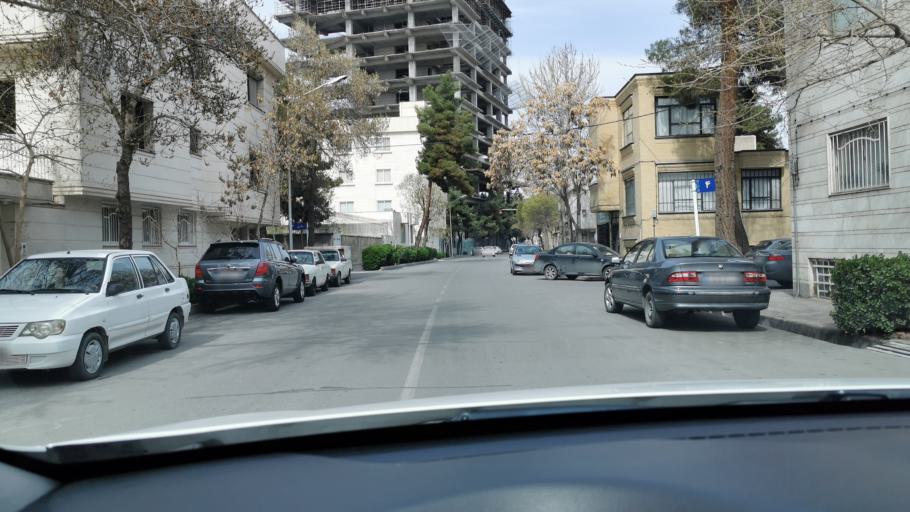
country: IR
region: Razavi Khorasan
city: Mashhad
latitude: 36.2941
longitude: 59.5750
